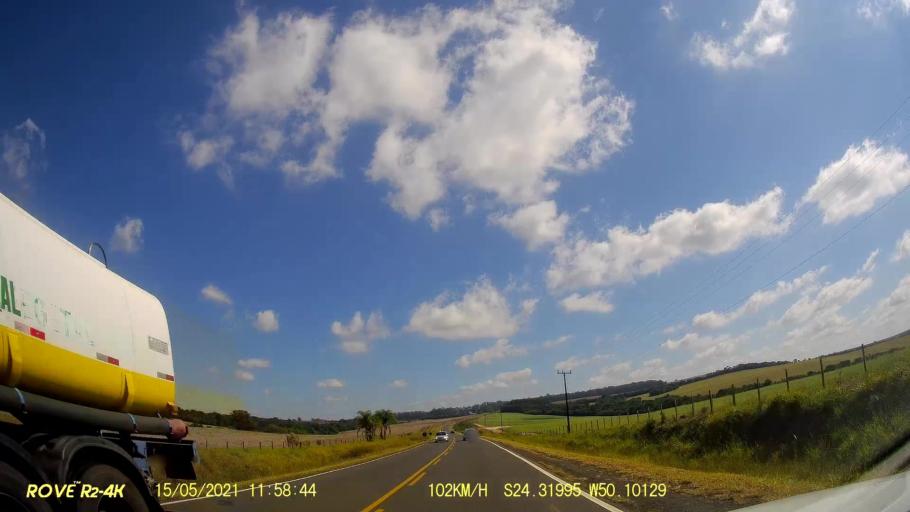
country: BR
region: Parana
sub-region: Pirai Do Sul
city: Pirai do Sul
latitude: -24.3204
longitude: -50.1017
